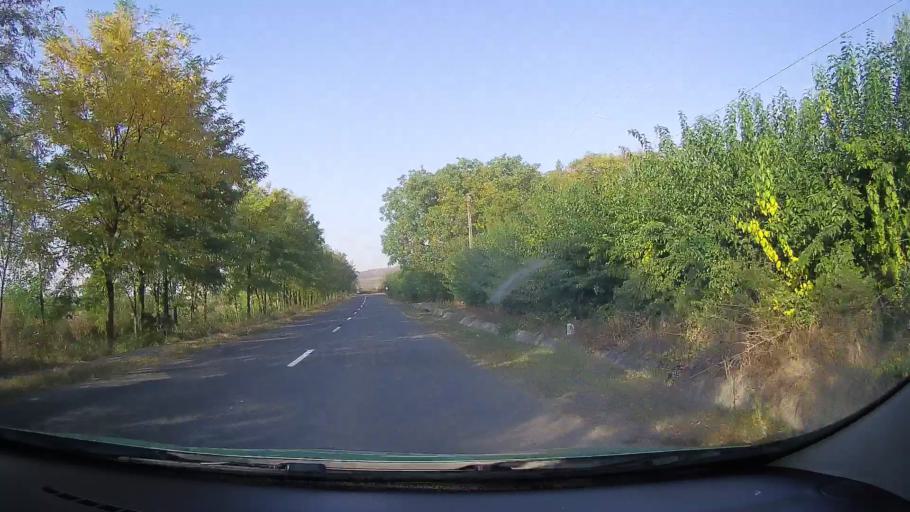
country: RO
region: Arad
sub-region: Comuna Paulis
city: Paulis
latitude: 46.1271
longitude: 21.5996
